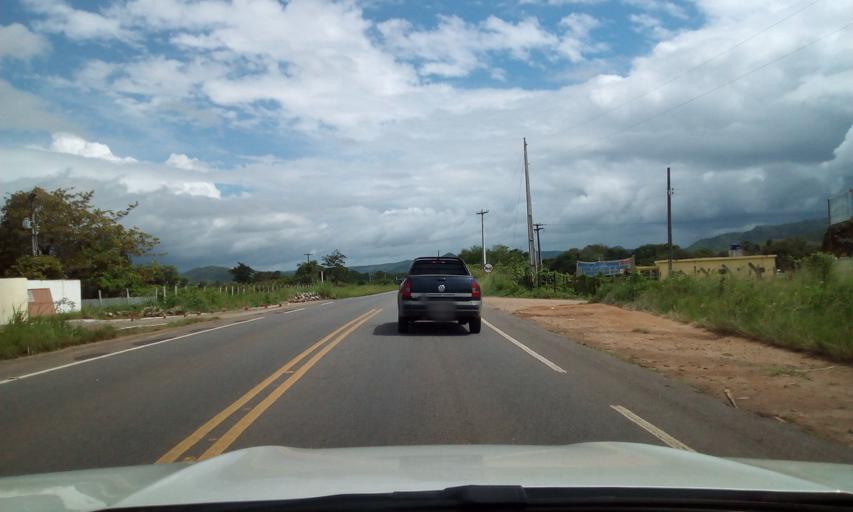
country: BR
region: Paraiba
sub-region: Guarabira
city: Guarabira
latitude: -6.8825
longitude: -35.5033
